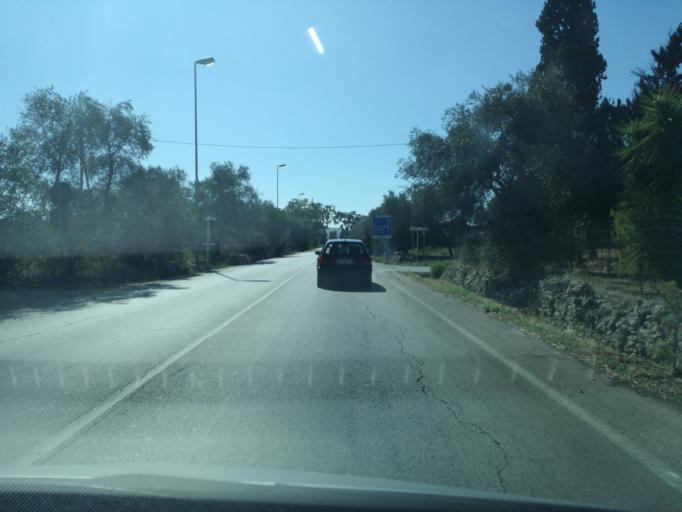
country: IT
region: Apulia
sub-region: Provincia di Bari
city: Capurso
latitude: 41.0538
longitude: 16.9156
